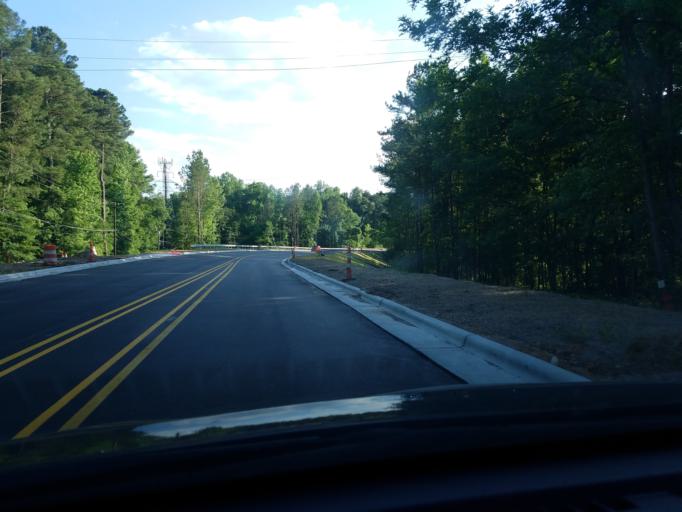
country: US
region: North Carolina
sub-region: Orange County
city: Chapel Hill
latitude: 35.9442
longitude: -78.9741
